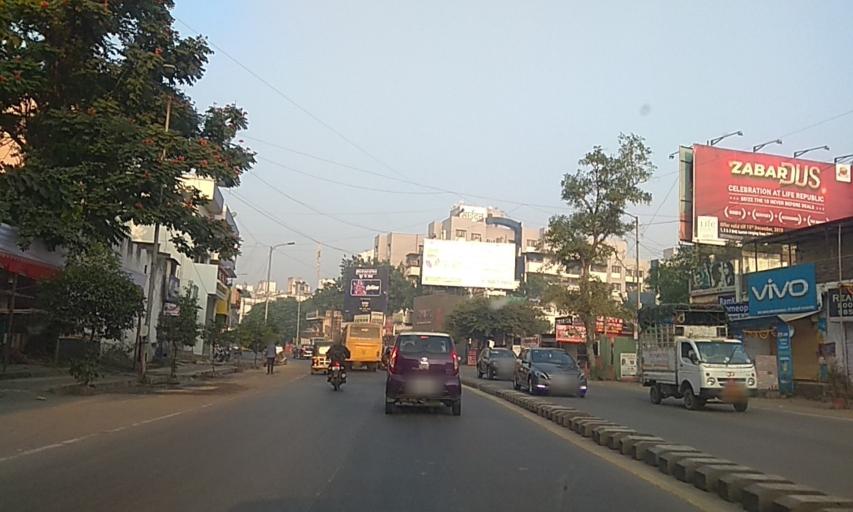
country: IN
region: Maharashtra
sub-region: Pune Division
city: Khadki
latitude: 18.5612
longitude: 73.7875
